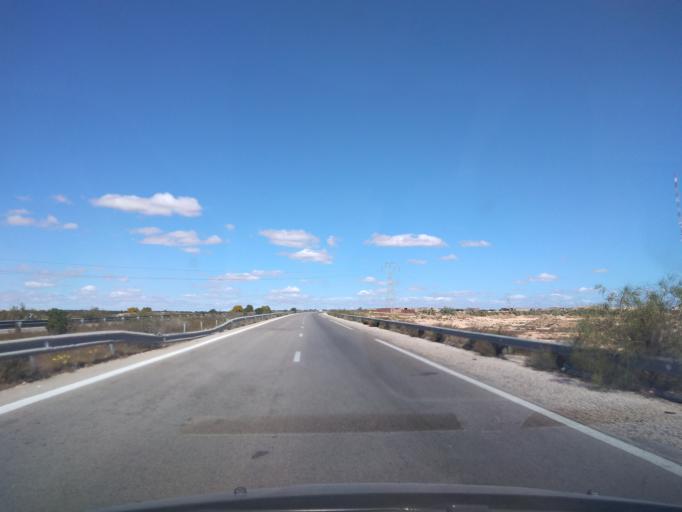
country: TN
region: Safaqis
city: Jabinyanah
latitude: 34.9407
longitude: 10.7367
